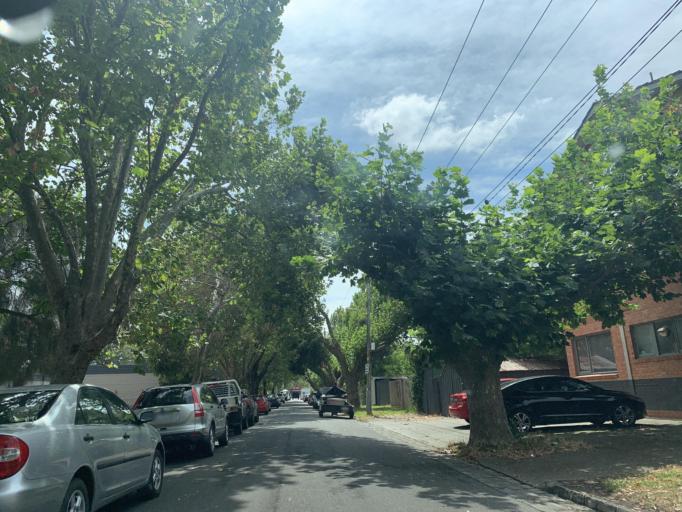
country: AU
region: Victoria
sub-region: Port Phillip
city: Elwood
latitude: -37.8820
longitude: 144.9886
